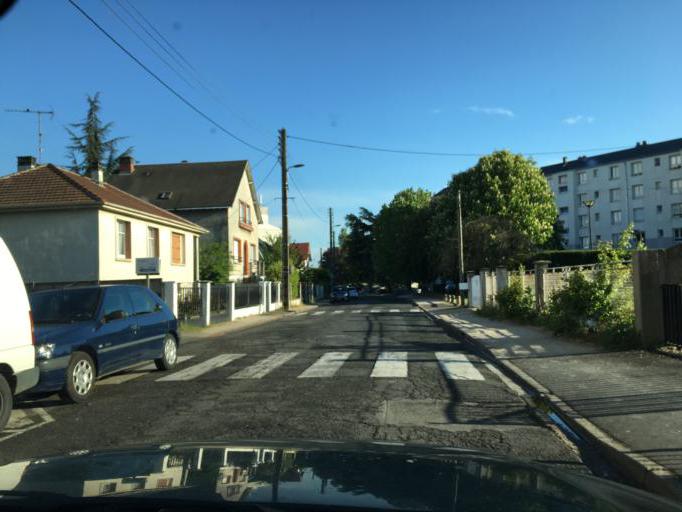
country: FR
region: Centre
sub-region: Departement du Loiret
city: Fleury-les-Aubrais
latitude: 47.9319
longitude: 1.9081
